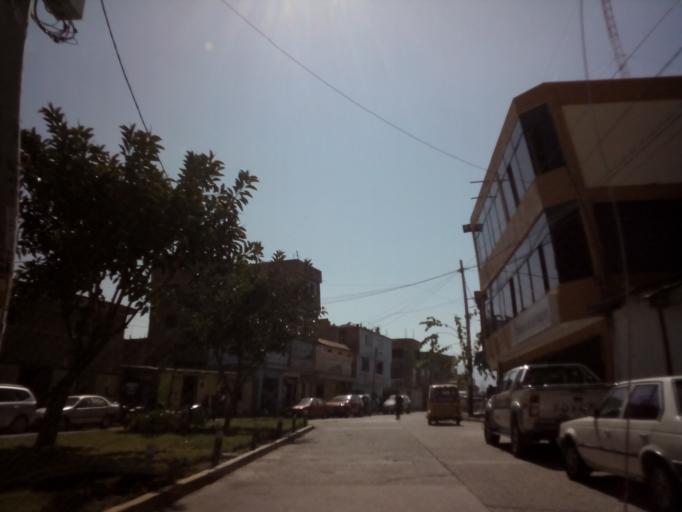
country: PE
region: Ayacucho
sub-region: Provincia de Huamanga
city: Ayacucho
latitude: -13.1562
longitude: -74.2179
